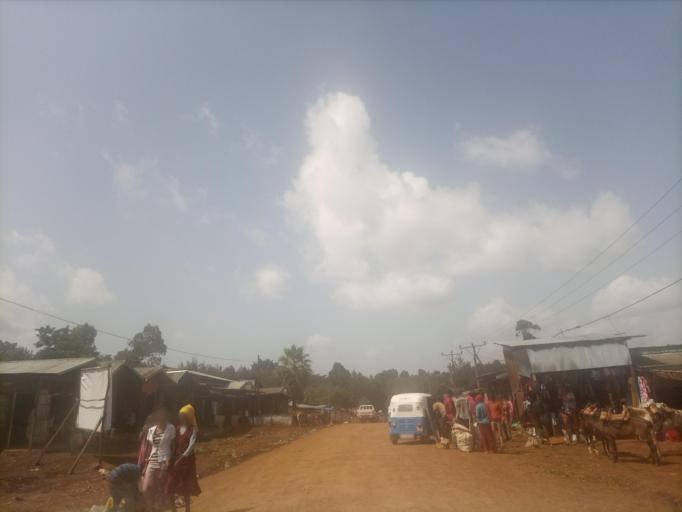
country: ET
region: Oromiya
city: Agaro
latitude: 7.7876
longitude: 36.4214
